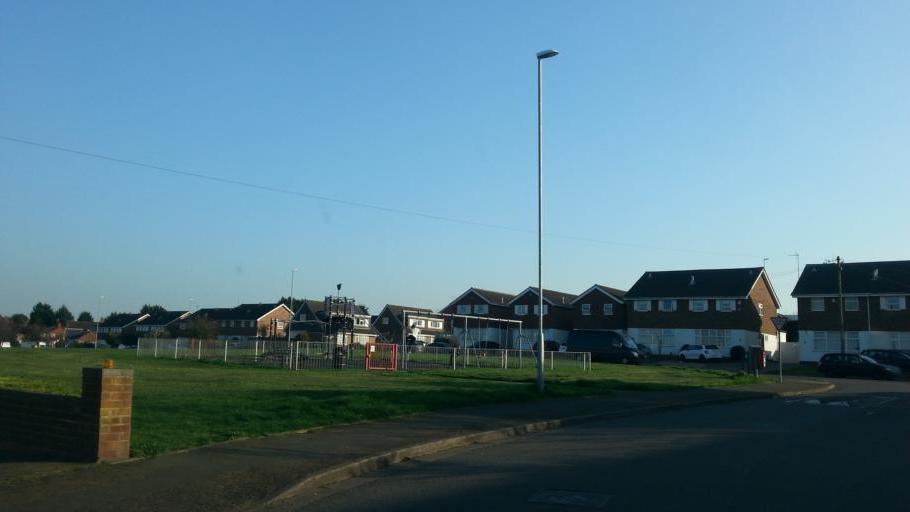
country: GB
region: England
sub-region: Northamptonshire
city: Rushden
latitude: 52.2922
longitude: -0.6198
